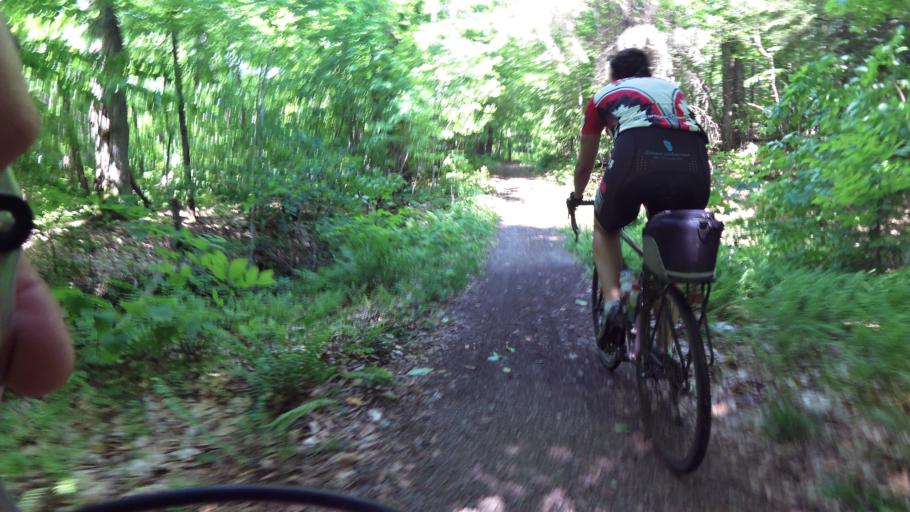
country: CA
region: Quebec
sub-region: Outaouais
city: Wakefield
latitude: 45.5576
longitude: -75.9022
